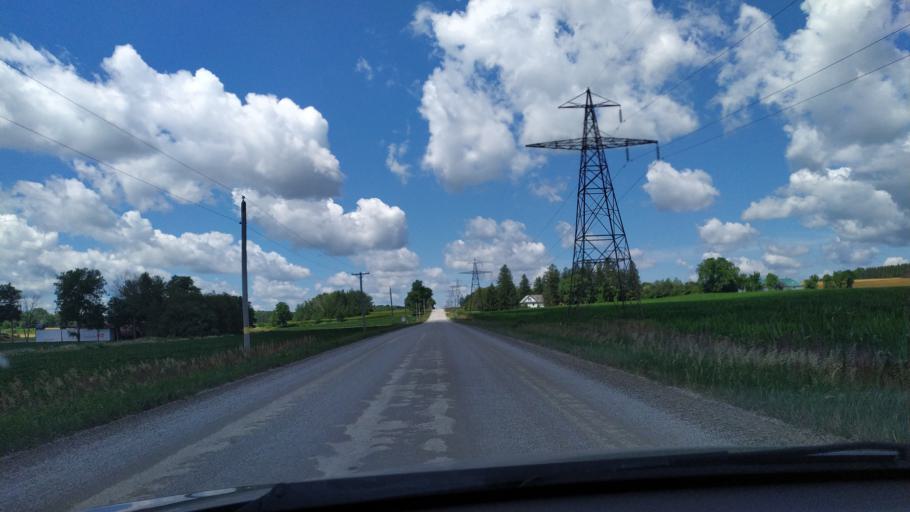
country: CA
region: Ontario
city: Stratford
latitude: 43.3874
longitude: -80.7774
